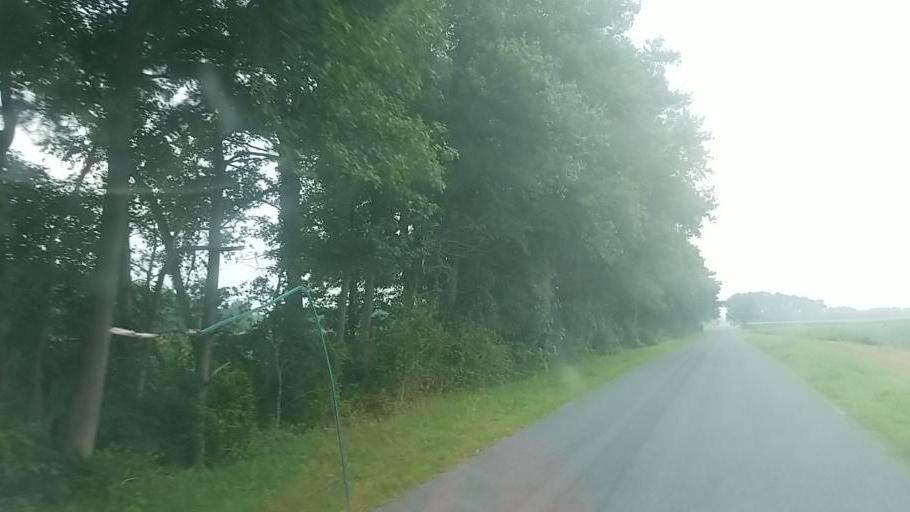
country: US
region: Maryland
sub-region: Wicomico County
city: Pittsville
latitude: 38.4521
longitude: -75.3747
